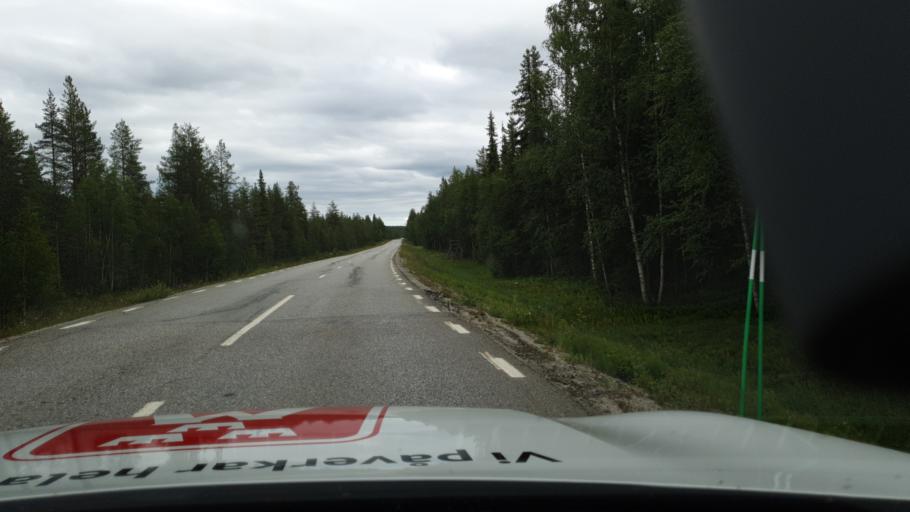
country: SE
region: Vaesterbotten
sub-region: Lycksele Kommun
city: Soderfors
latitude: 64.6955
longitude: 17.7467
